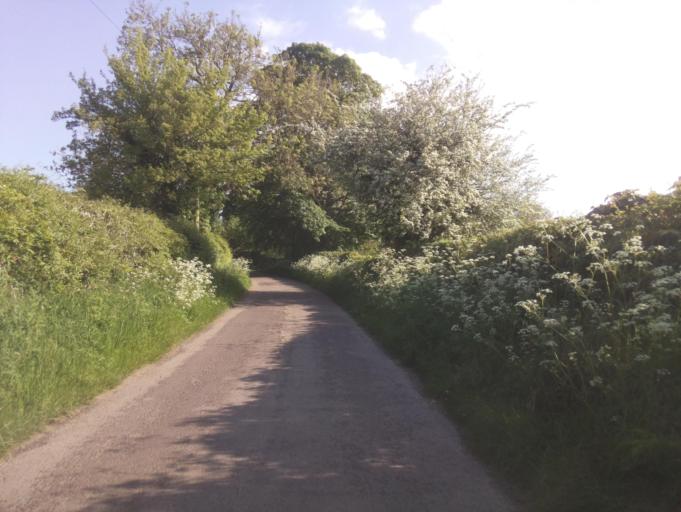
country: GB
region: England
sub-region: Wiltshire
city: Biddestone
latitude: 51.4765
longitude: -2.2061
